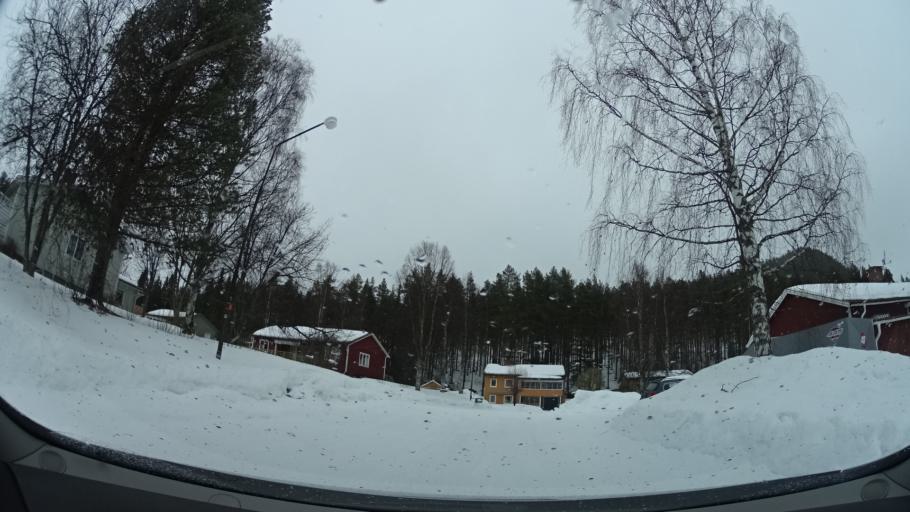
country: SE
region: Vaesterbotten
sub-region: Mala Kommun
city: Mala
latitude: 65.1766
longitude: 18.7513
